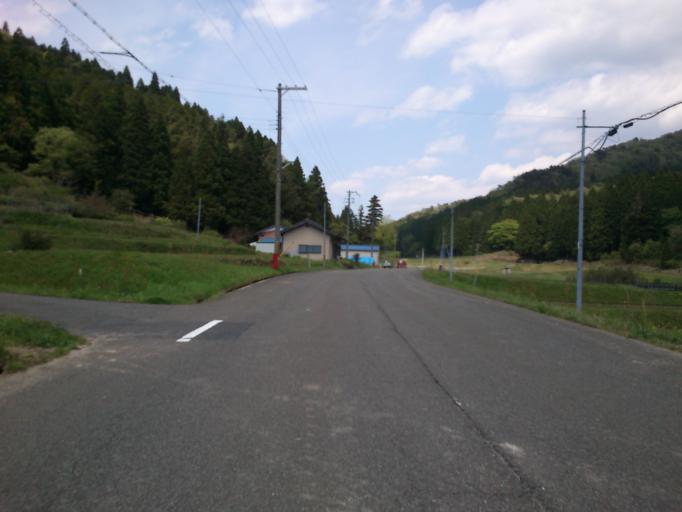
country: JP
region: Kyoto
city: Fukuchiyama
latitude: 35.3790
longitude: 134.9385
